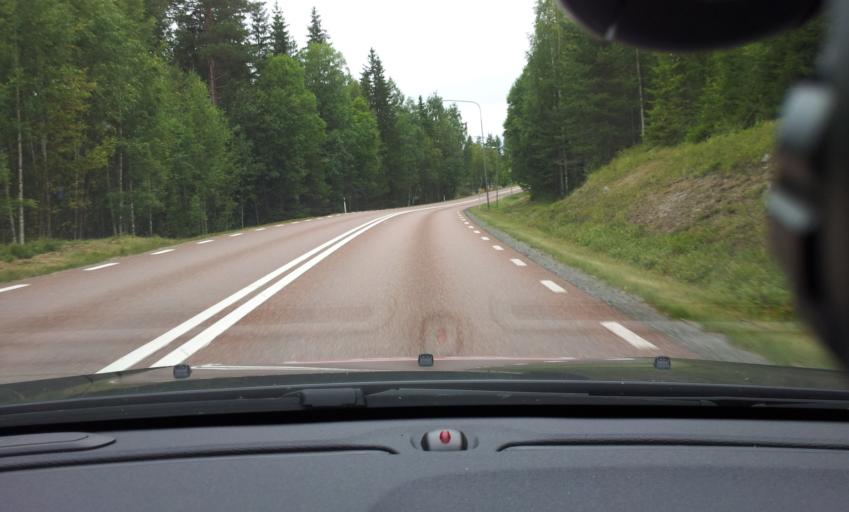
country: SE
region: Jaemtland
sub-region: OEstersunds Kommun
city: Brunflo
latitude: 62.9484
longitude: 15.0543
